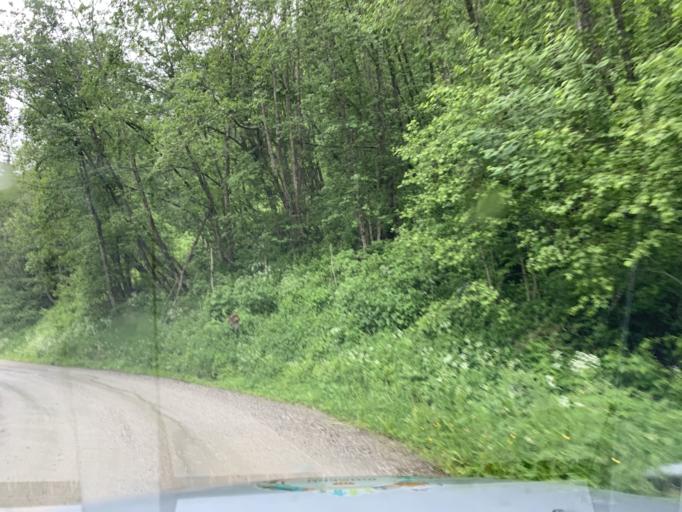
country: NO
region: Oppland
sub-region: Oyer
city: Tretten
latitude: 61.3935
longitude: 10.2740
